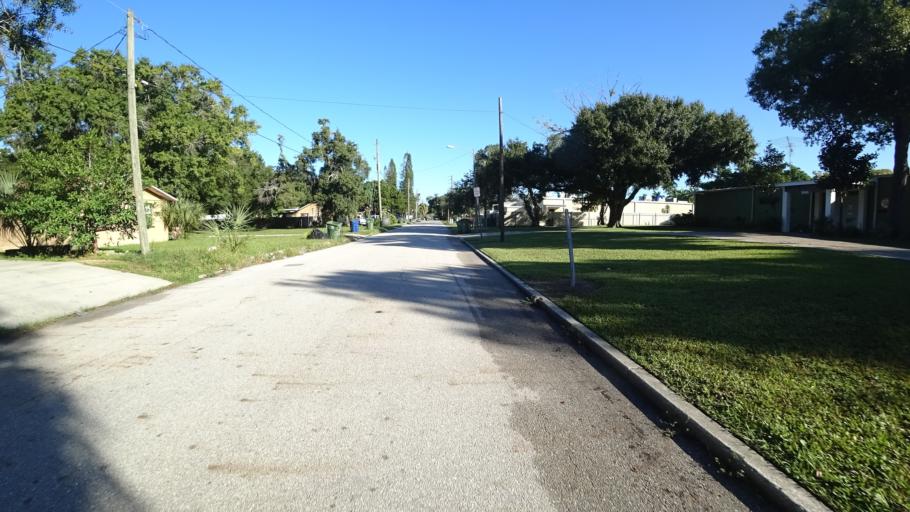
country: US
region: Florida
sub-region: Manatee County
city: Bradenton
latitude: 27.4822
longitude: -82.5726
